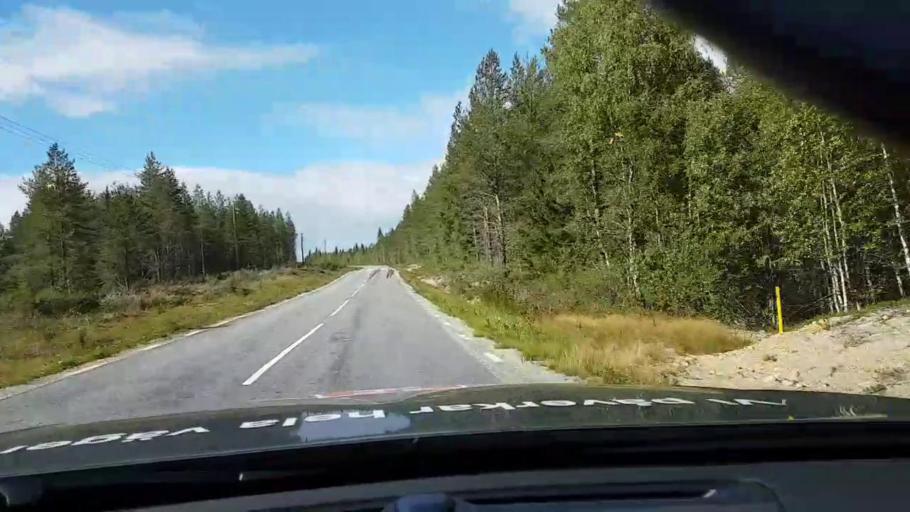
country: SE
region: Vaesterbotten
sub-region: Asele Kommun
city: Asele
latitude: 63.8180
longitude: 17.4939
